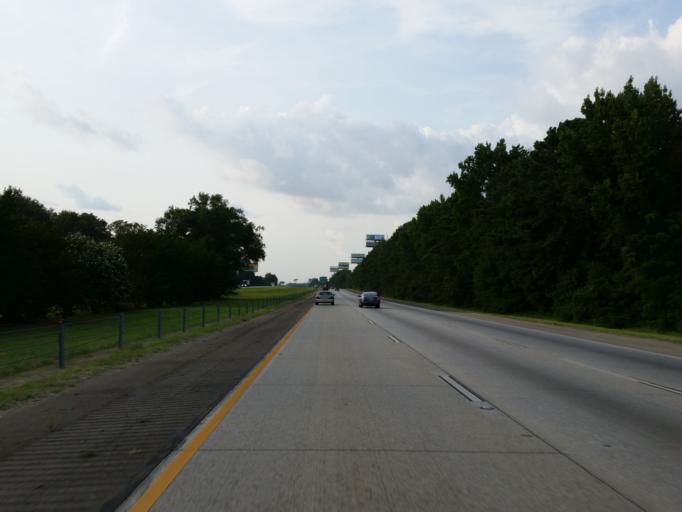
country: US
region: Georgia
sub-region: Peach County
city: Byron
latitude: 32.5963
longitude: -83.7426
